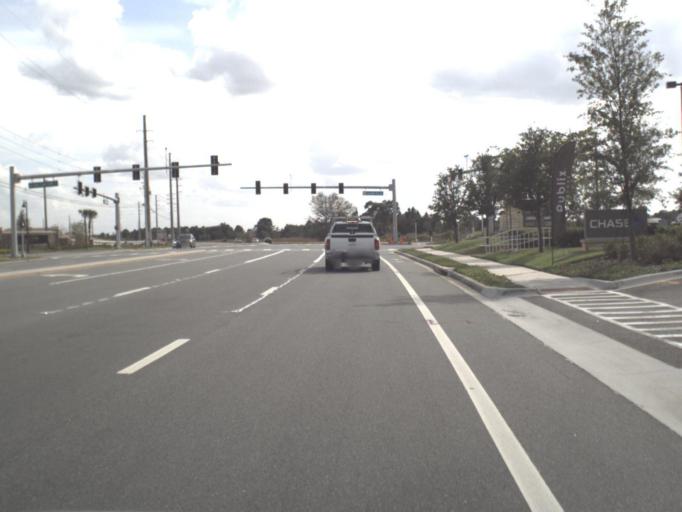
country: US
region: Florida
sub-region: Osceola County
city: Buenaventura Lakes
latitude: 28.3647
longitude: -81.2446
